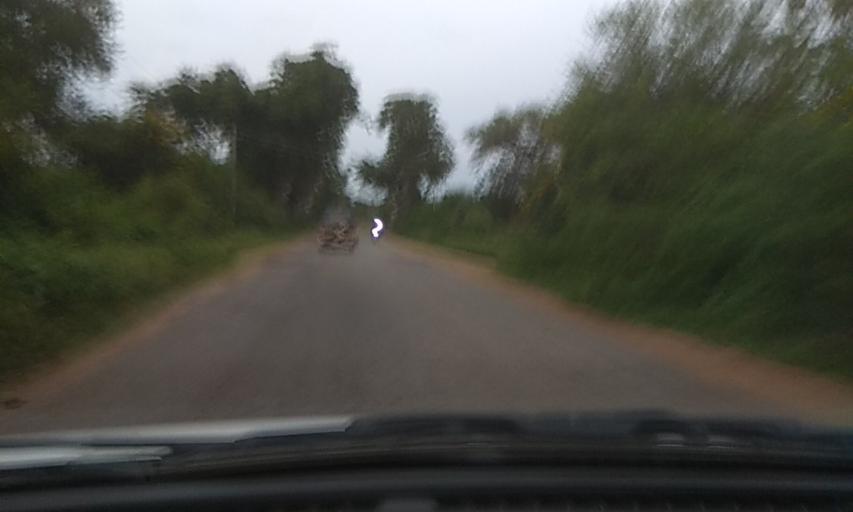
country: IN
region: Karnataka
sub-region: Chamrajnagar
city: Gundlupet
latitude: 11.8136
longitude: 76.7655
